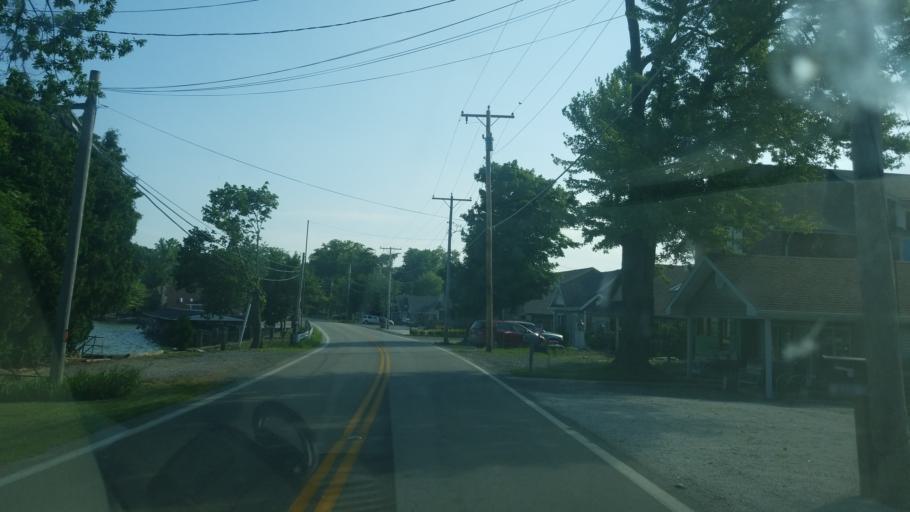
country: US
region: Ohio
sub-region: Logan County
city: Russells Point
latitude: 40.4906
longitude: -83.8595
